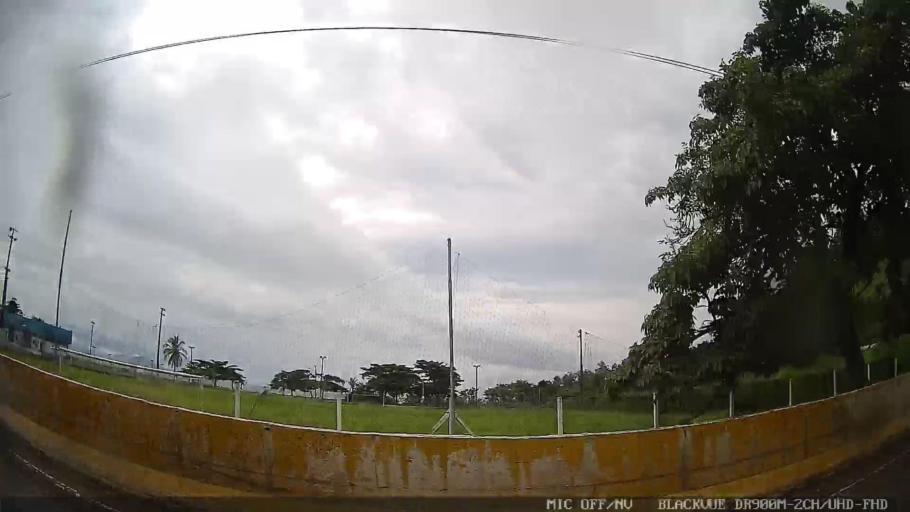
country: BR
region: Sao Paulo
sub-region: Sao Sebastiao
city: Sao Sebastiao
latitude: -23.7247
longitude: -45.4241
